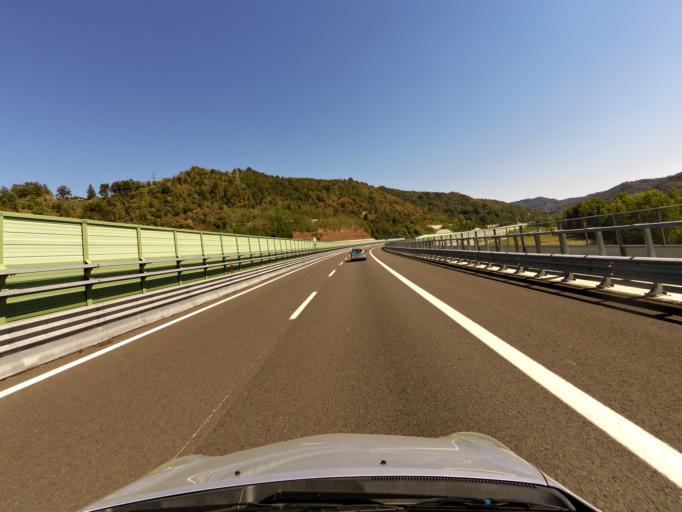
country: IT
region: Emilia-Romagna
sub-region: Provincia di Bologna
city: Marzabotto
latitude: 44.2907
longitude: 11.2103
